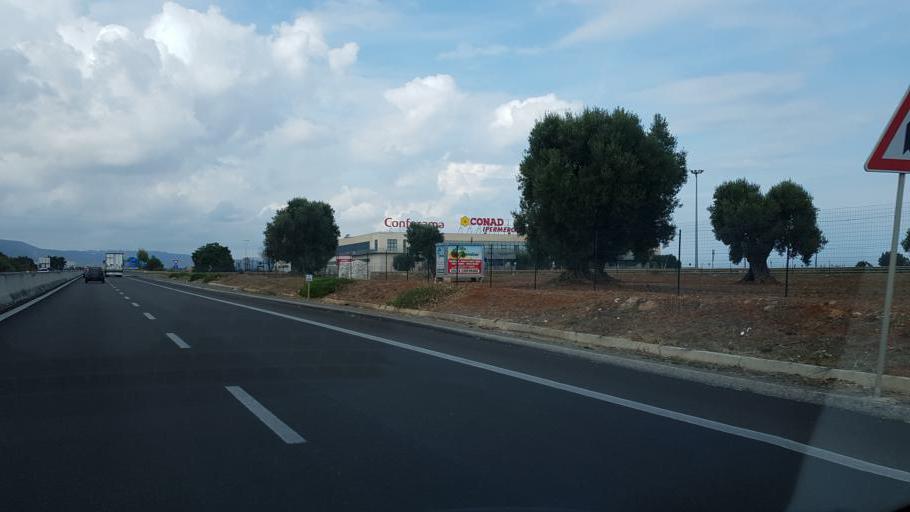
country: IT
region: Apulia
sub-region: Provincia di Brindisi
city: Fasano
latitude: 40.8375
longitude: 17.3818
